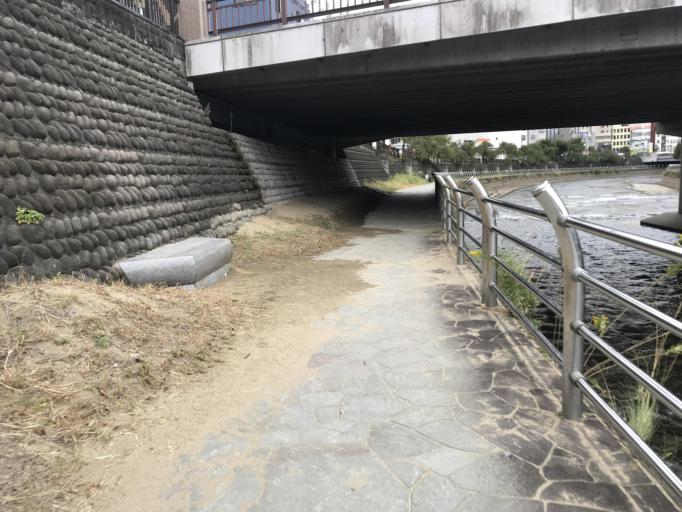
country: JP
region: Tochigi
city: Utsunomiya-shi
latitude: 36.5619
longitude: 139.8954
